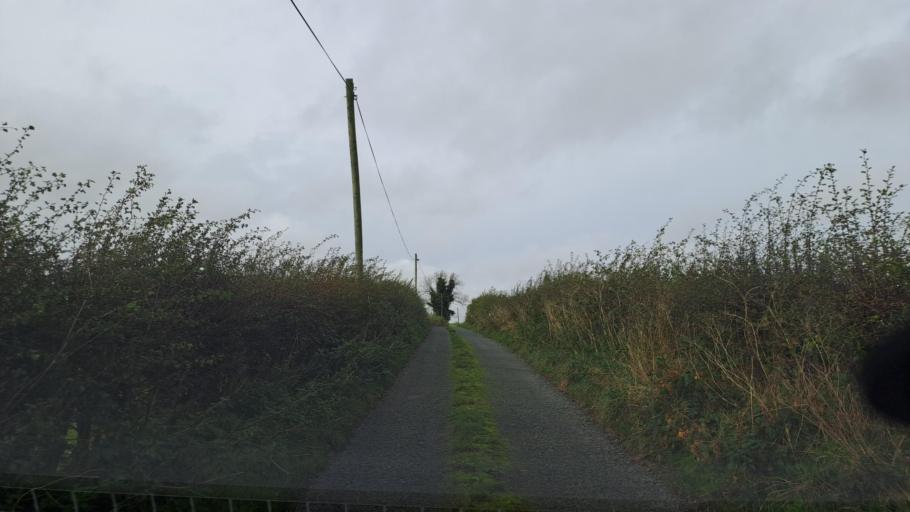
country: IE
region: Ulster
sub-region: County Monaghan
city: Carrickmacross
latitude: 54.0146
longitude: -6.8087
